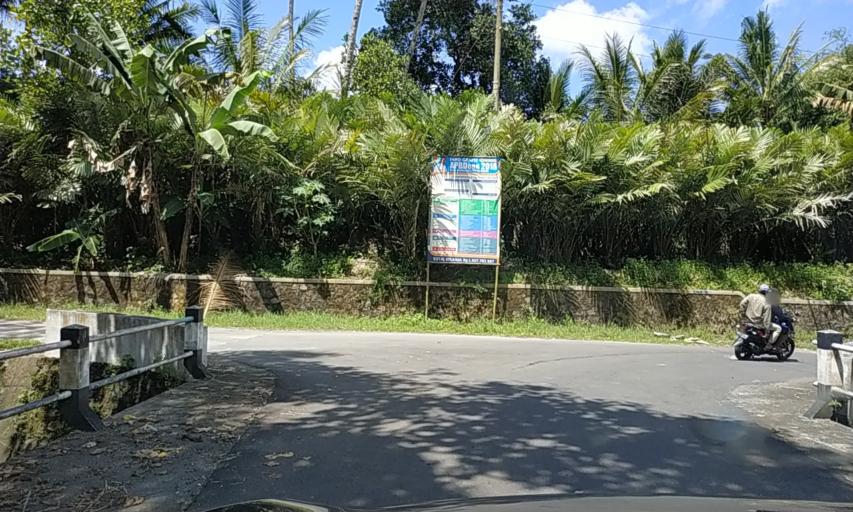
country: ID
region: Central Java
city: Muntilan
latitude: -7.5724
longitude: 110.3364
